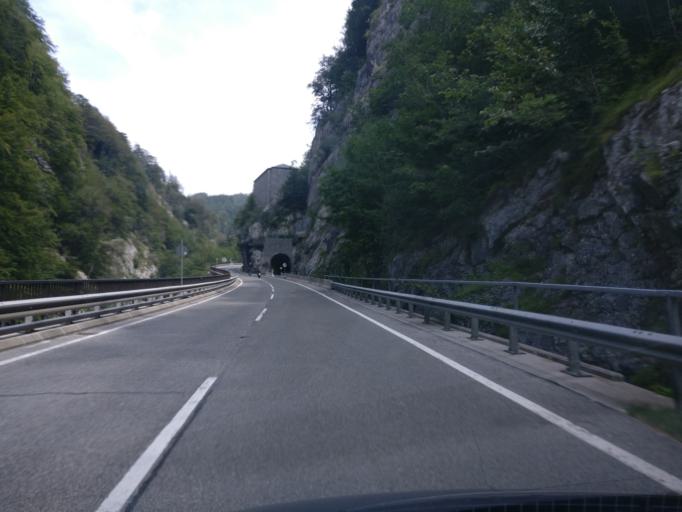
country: AT
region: Salzburg
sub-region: Politischer Bezirk Hallein
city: Golling an der Salzach
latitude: 47.5681
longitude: 13.1848
